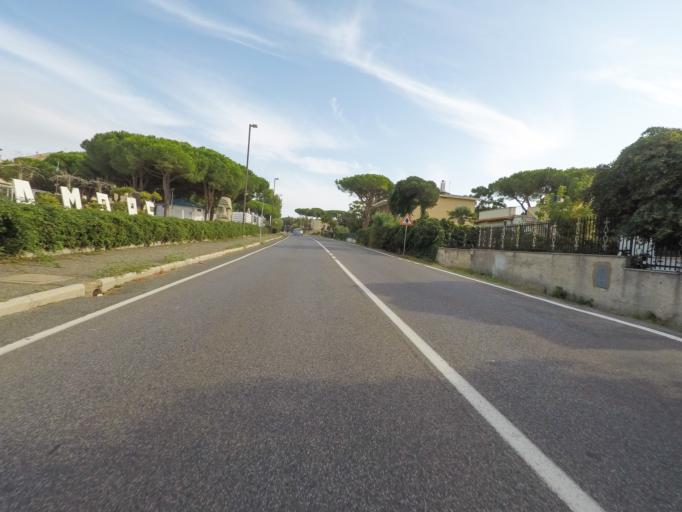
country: IT
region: Latium
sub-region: Citta metropolitana di Roma Capitale
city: Santa Marinella
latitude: 42.0348
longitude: 11.8344
